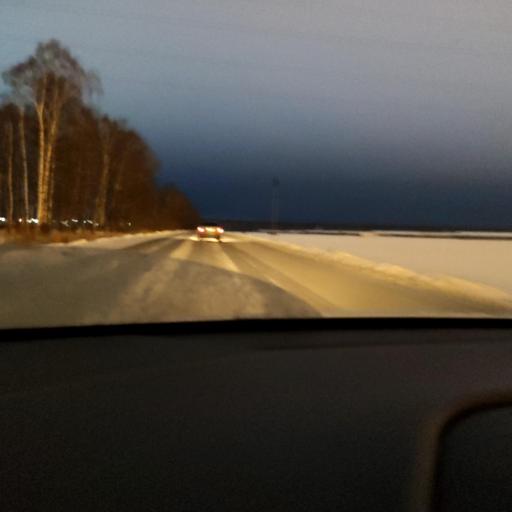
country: RU
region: Tatarstan
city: Osinovo
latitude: 55.8882
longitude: 48.8910
